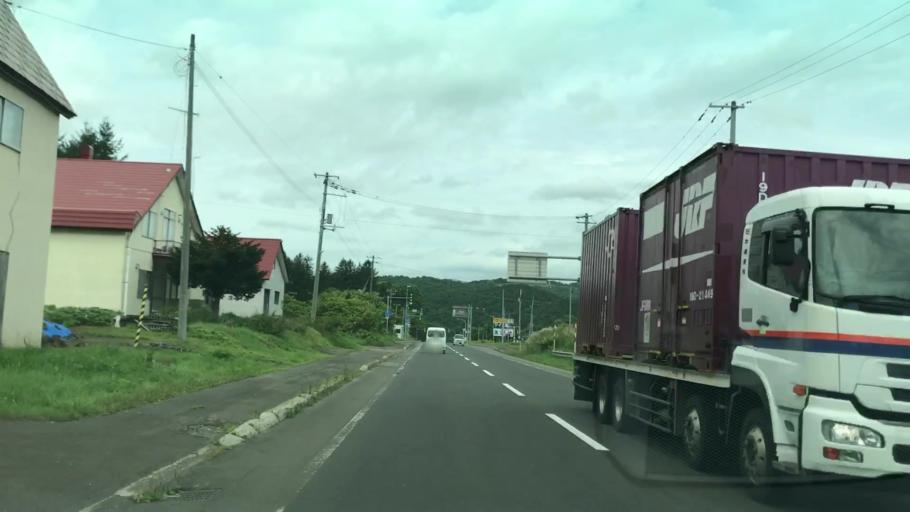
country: JP
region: Hokkaido
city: Niseko Town
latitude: 42.9580
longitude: 140.6953
